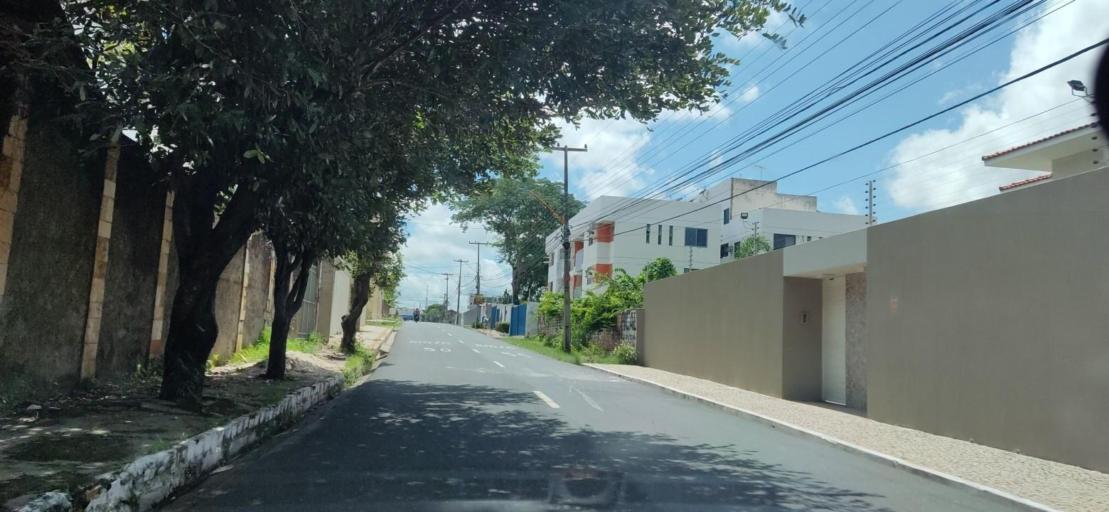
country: BR
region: Piaui
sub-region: Teresina
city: Teresina
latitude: -5.0661
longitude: -42.7741
